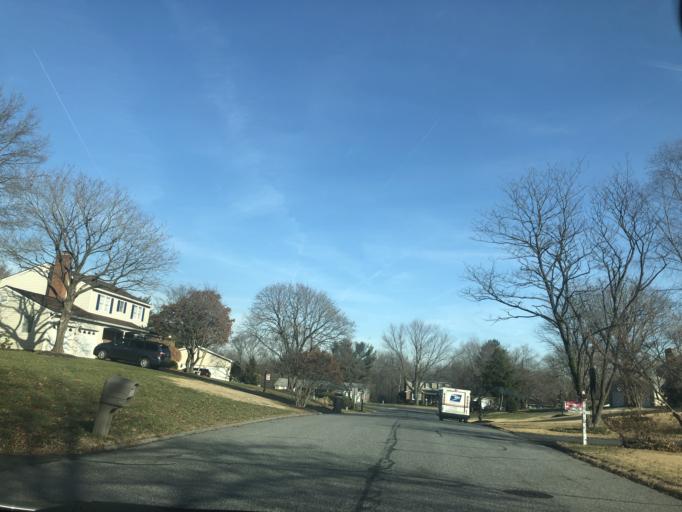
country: US
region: Maryland
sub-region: Howard County
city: Columbia
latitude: 39.2880
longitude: -76.8486
